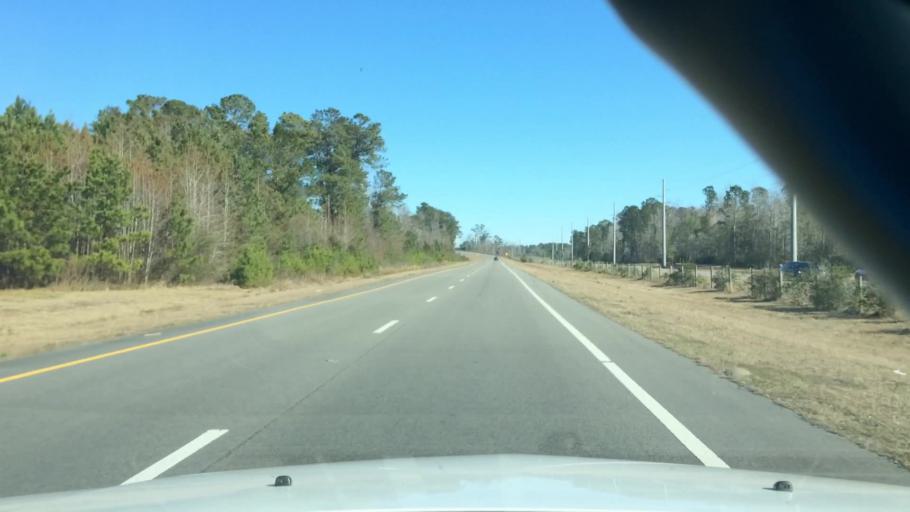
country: US
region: North Carolina
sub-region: Brunswick County
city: Leland
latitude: 34.1837
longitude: -78.0819
